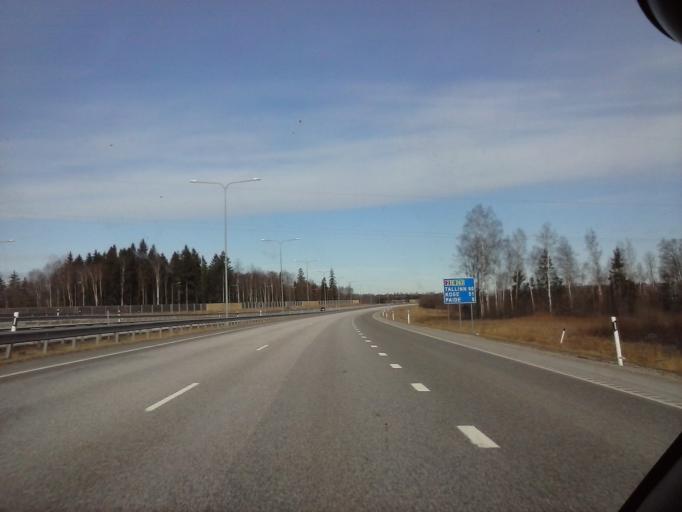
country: EE
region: Jaervamaa
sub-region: Paide linn
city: Paide
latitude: 58.9009
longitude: 25.6399
